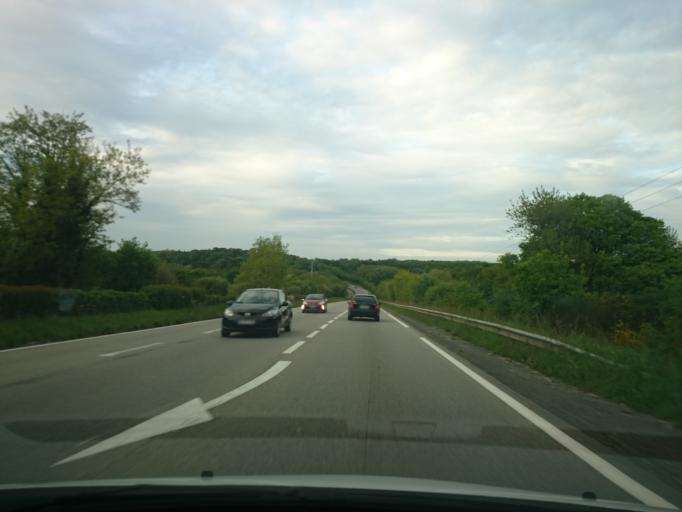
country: FR
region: Pays de la Loire
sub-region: Departement de la Loire-Atlantique
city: Saint-Herblain
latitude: 47.2401
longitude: -1.6394
